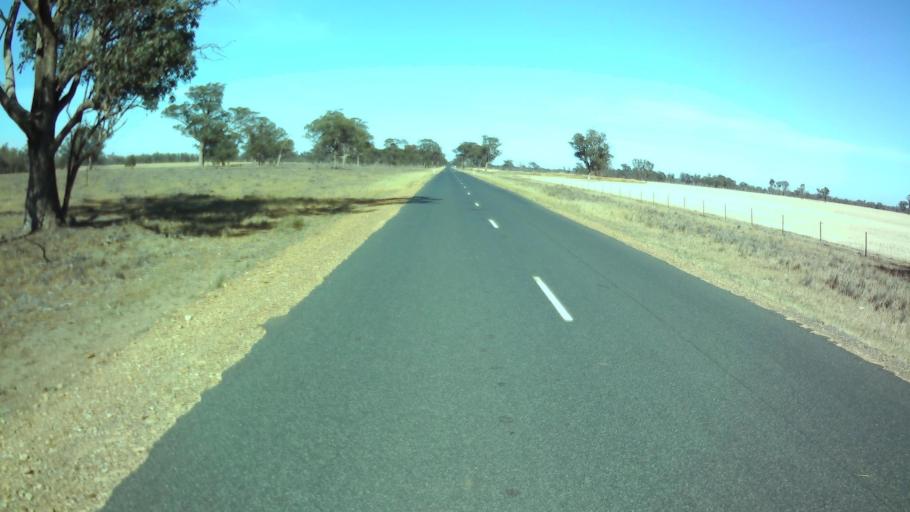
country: AU
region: New South Wales
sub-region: Weddin
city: Grenfell
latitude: -34.1361
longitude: 147.7731
